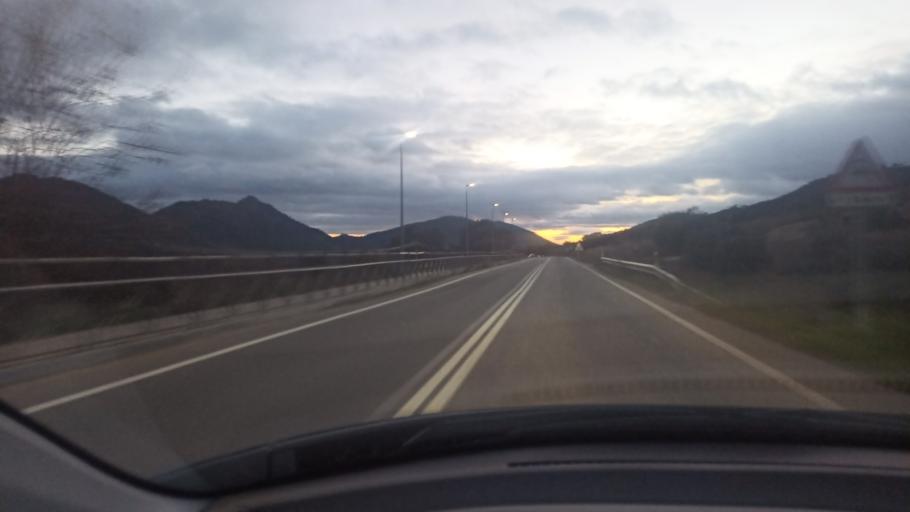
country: ES
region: Madrid
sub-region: Provincia de Madrid
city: Robledo de Chavela
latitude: 40.4918
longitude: -4.2445
